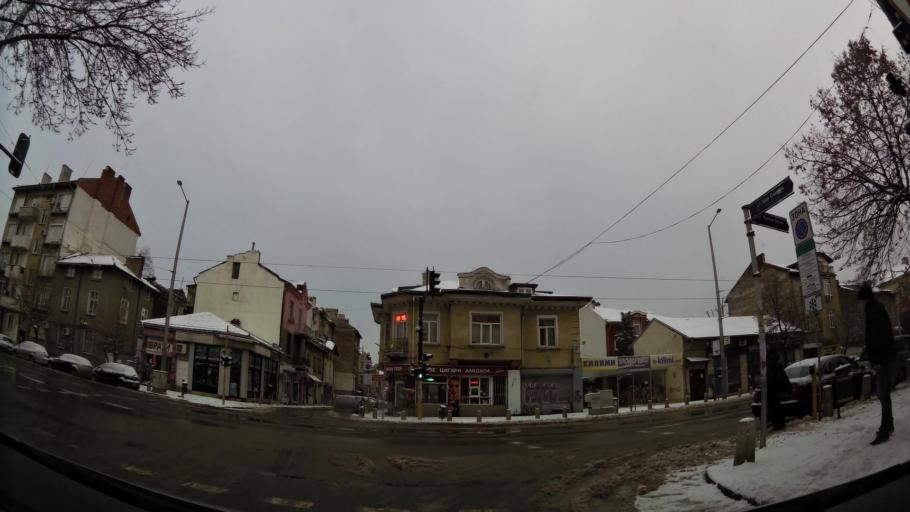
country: BG
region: Sofia-Capital
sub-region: Stolichna Obshtina
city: Sofia
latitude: 42.7022
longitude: 23.3165
